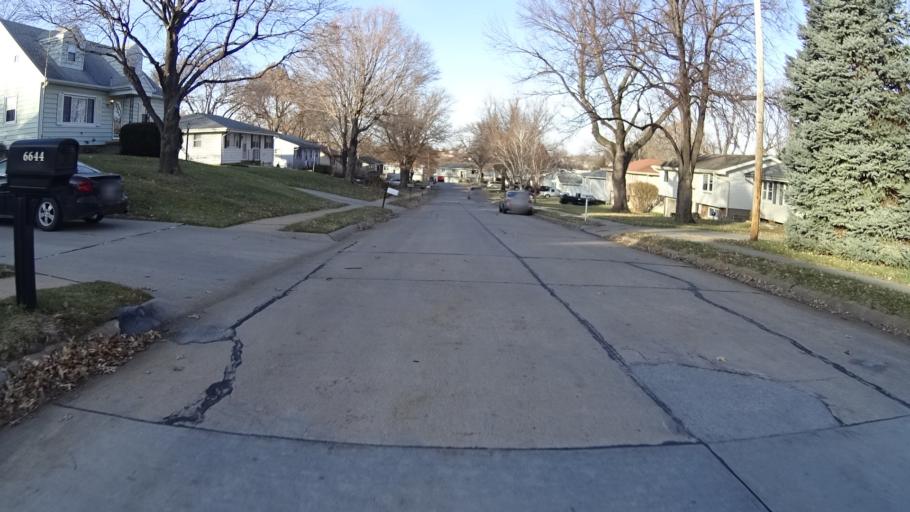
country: US
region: Nebraska
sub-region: Douglas County
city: Ralston
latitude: 41.1925
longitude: -96.0472
